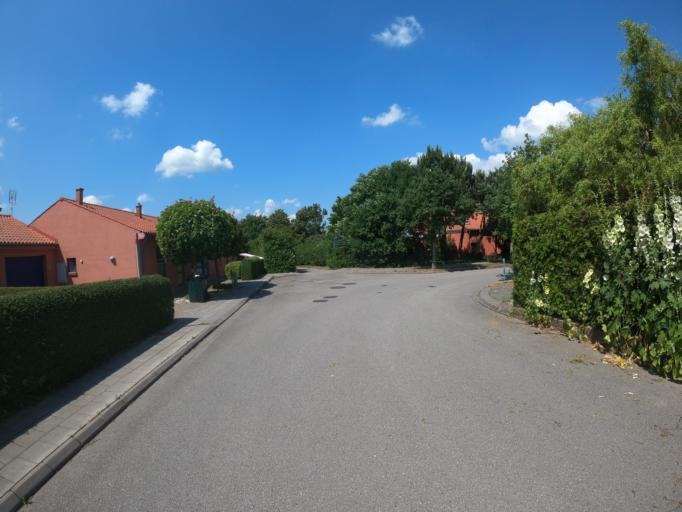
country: SE
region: Skane
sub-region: Lunds Kommun
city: Lund
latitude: 55.7018
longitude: 13.1568
